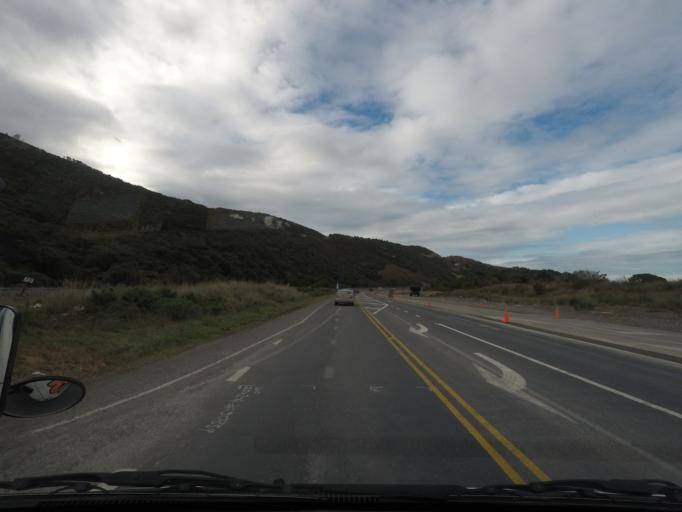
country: NZ
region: Canterbury
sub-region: Kaikoura District
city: Kaikoura
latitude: -42.2172
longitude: 173.8598
